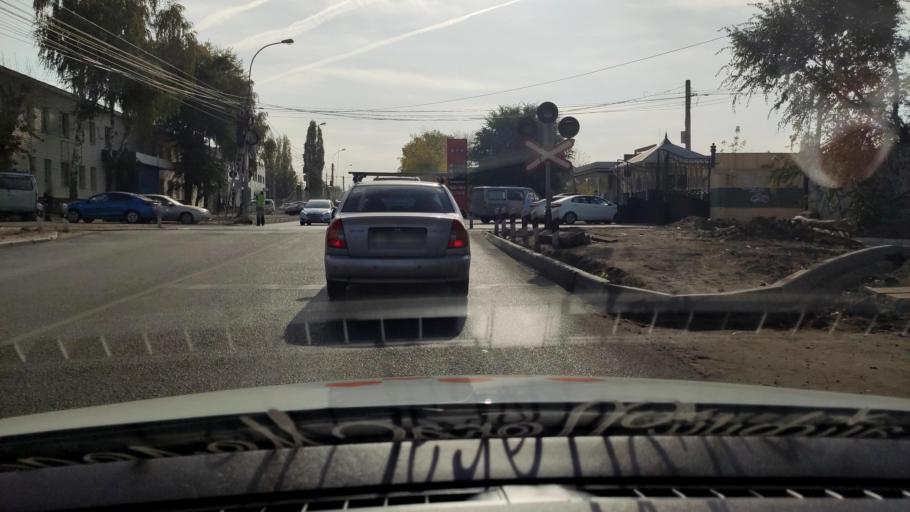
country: RU
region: Voronezj
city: Voronezh
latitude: 51.6658
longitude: 39.1505
